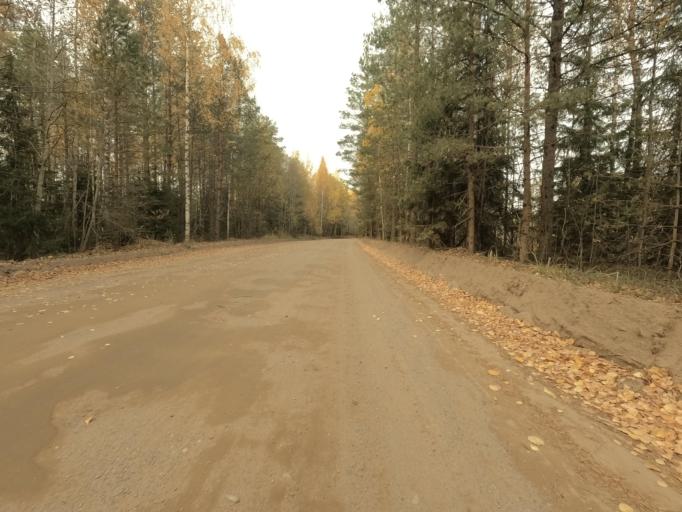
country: RU
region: Leningrad
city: Priladozhskiy
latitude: 59.6846
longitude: 31.3622
